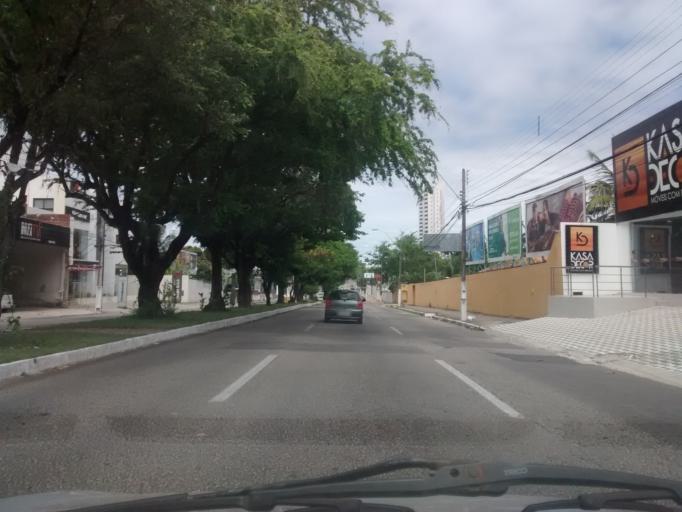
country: BR
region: Rio Grande do Norte
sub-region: Natal
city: Natal
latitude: -5.8022
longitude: -35.2068
